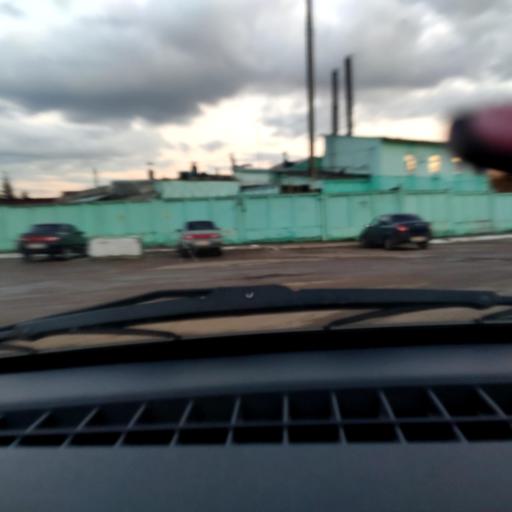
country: RU
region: Bashkortostan
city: Ufa
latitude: 54.8060
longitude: 56.0870
